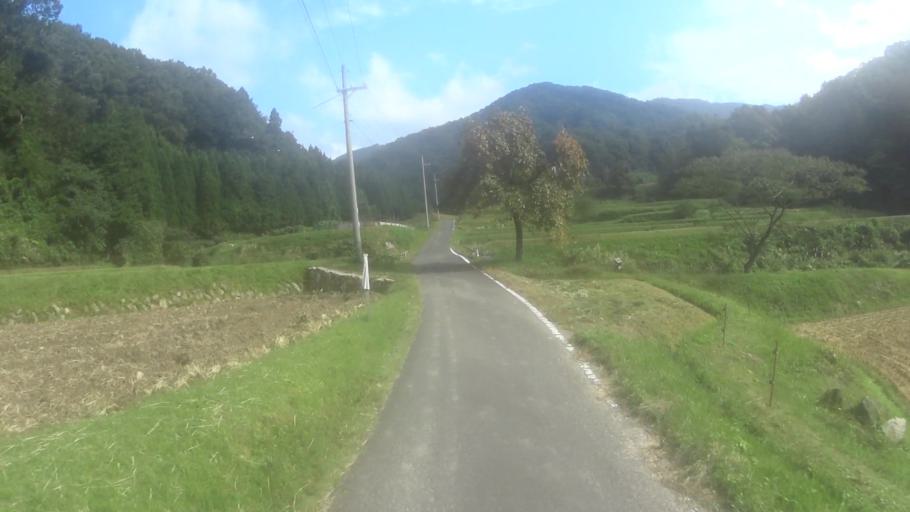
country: JP
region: Kyoto
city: Miyazu
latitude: 35.6144
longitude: 135.1527
